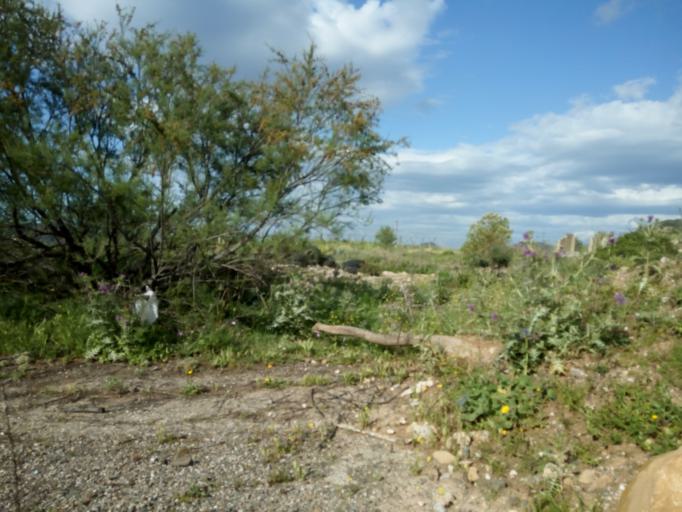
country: DZ
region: Tipaza
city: El Affroun
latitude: 36.3753
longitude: 2.5180
